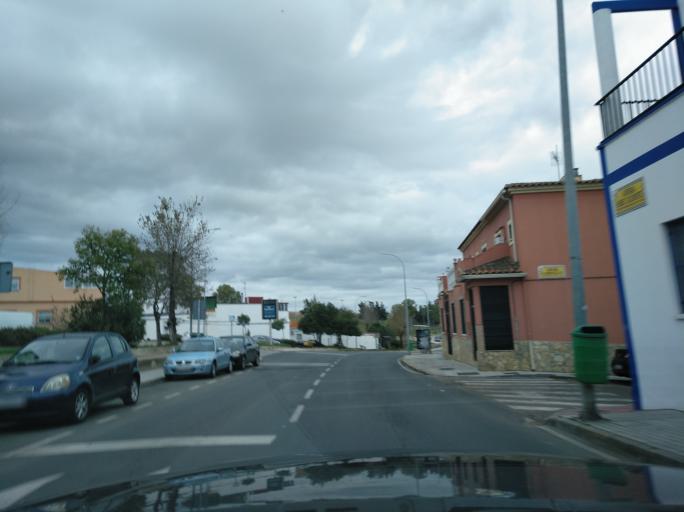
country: ES
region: Extremadura
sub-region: Provincia de Badajoz
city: Badajoz
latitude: 38.8905
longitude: -6.9770
